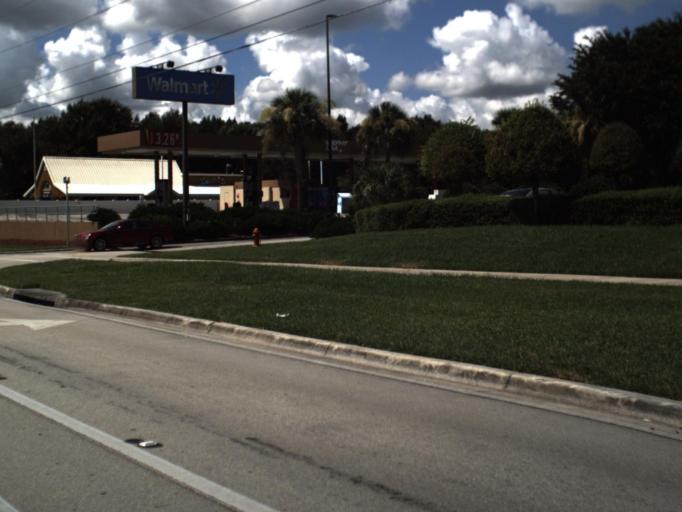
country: US
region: Florida
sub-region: Polk County
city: Gibsonia
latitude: 28.1184
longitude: -81.9738
